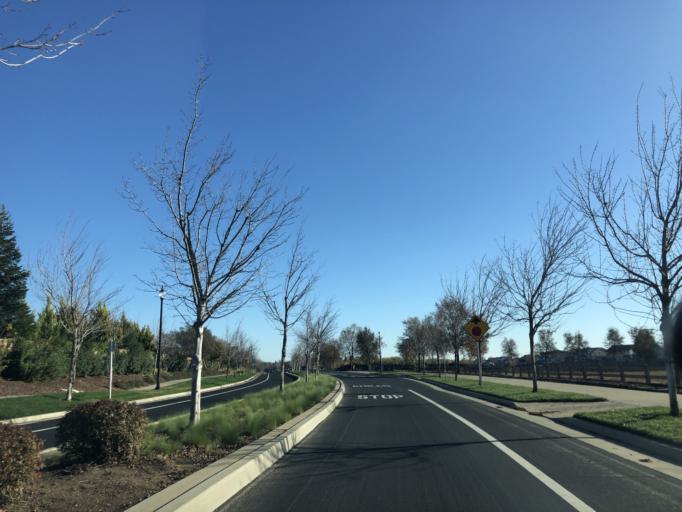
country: US
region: California
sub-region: Sacramento County
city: Antelope
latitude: 38.7868
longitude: -121.3692
